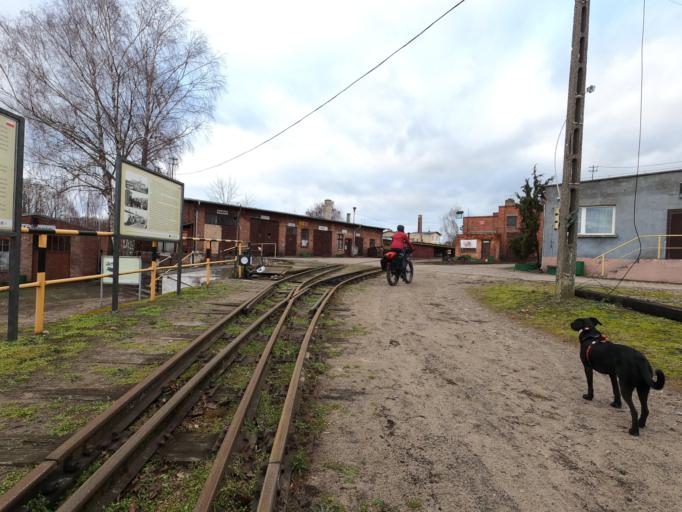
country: PL
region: Greater Poland Voivodeship
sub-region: Powiat pilski
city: Bialosliwie
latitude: 53.0968
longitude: 17.1171
